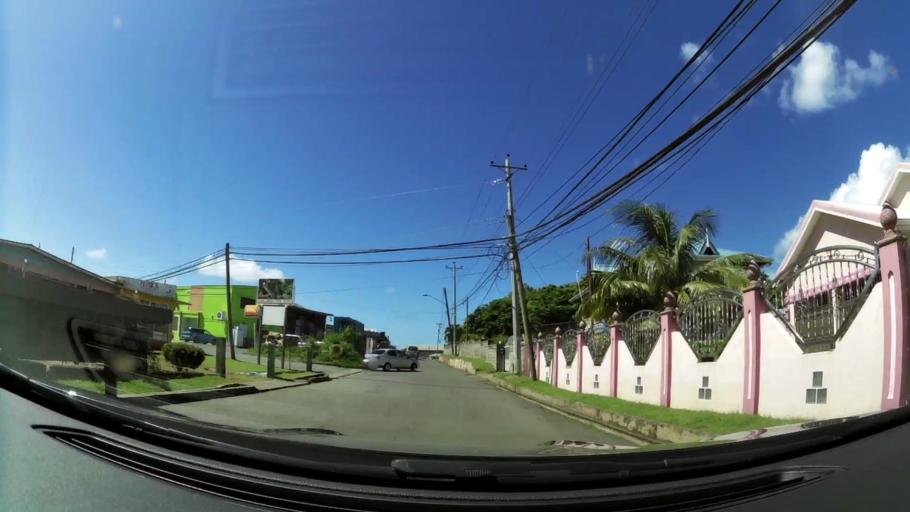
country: TT
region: Tobago
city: Scarborough
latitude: 11.1690
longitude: -60.7872
